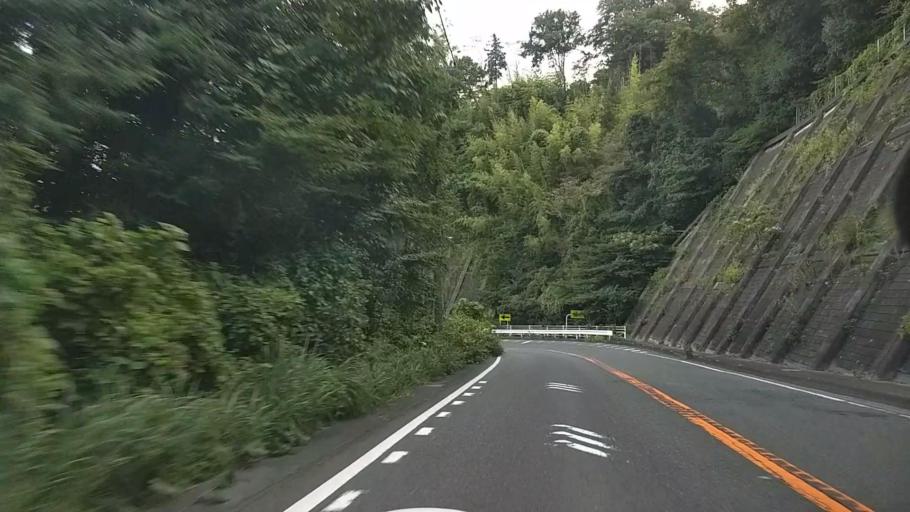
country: JP
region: Shizuoka
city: Fujinomiya
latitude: 35.3184
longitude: 138.4394
